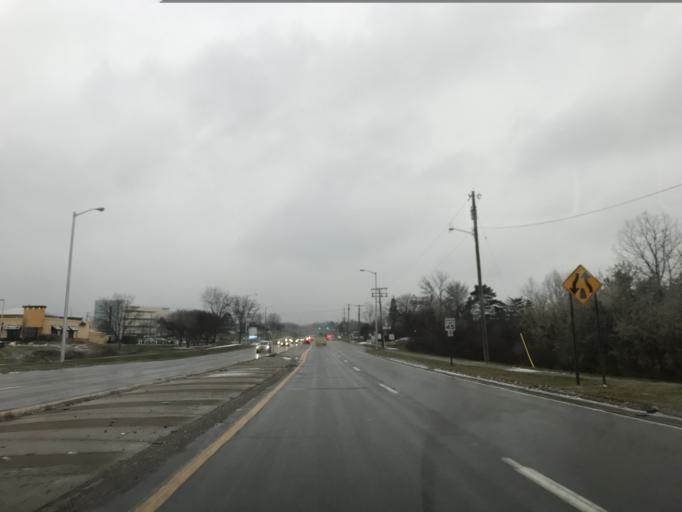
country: US
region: Michigan
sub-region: Wayne County
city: Northville
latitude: 42.4250
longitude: -83.4271
